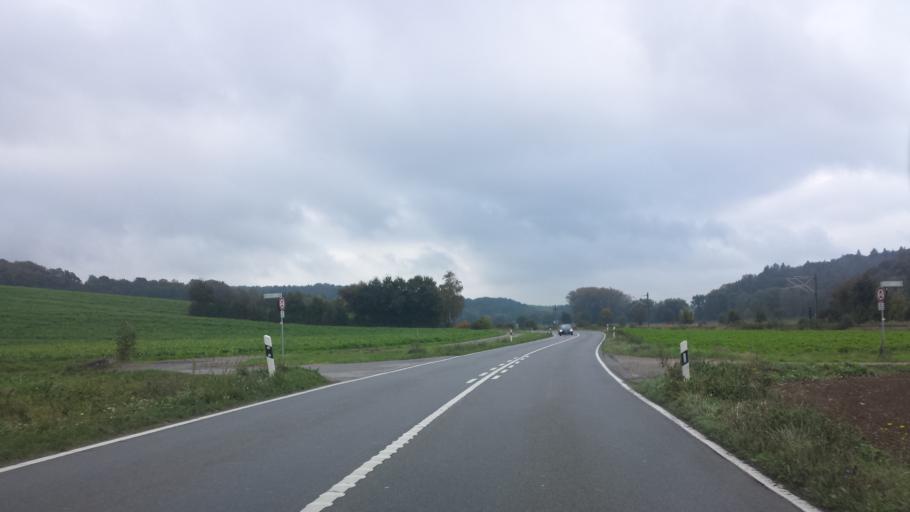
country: DE
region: Baden-Wuerttemberg
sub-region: Regierungsbezirk Stuttgart
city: Ittlingen
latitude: 49.2139
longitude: 8.9255
